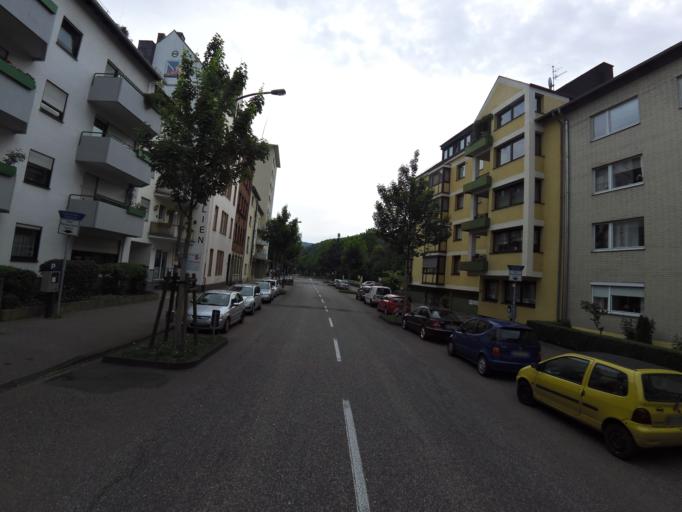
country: DE
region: Rheinland-Pfalz
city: Koblenz
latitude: 50.3423
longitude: 7.5869
